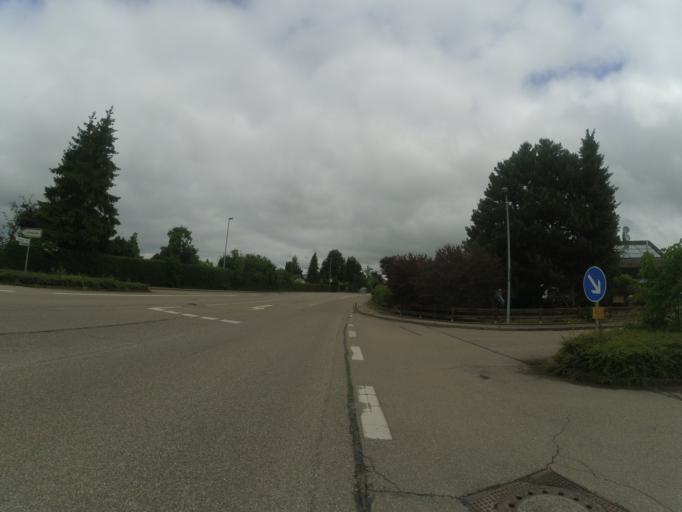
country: DE
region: Baden-Wuerttemberg
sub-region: Tuebingen Region
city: Bernstadt
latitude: 48.4952
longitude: 10.0265
